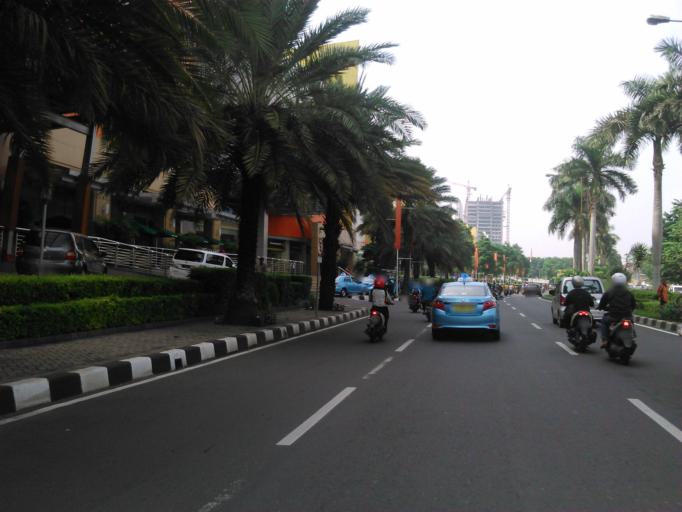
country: ID
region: East Java
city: Mulyorejo
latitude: -7.2740
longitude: 112.7818
